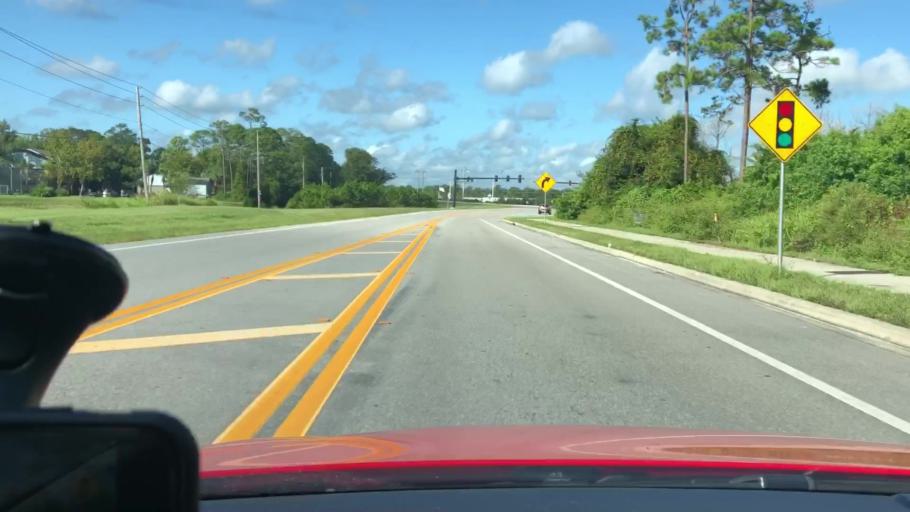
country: US
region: Florida
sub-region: Volusia County
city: Holly Hill
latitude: 29.2014
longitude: -81.0889
